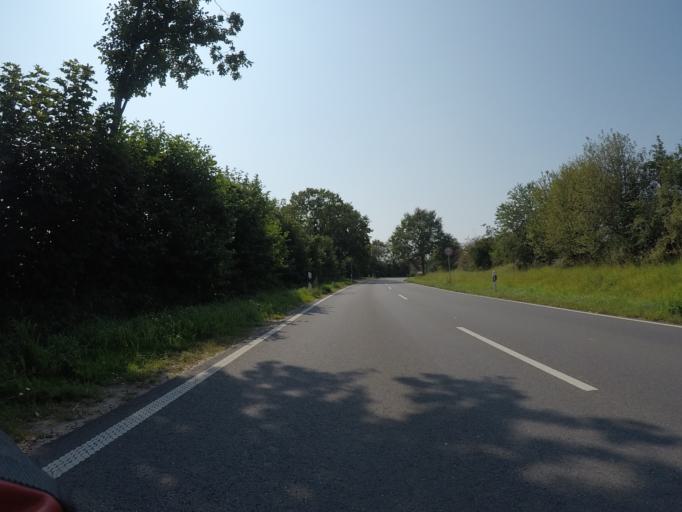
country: DE
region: Schleswig-Holstein
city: Sievershutten
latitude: 53.8408
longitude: 10.0959
